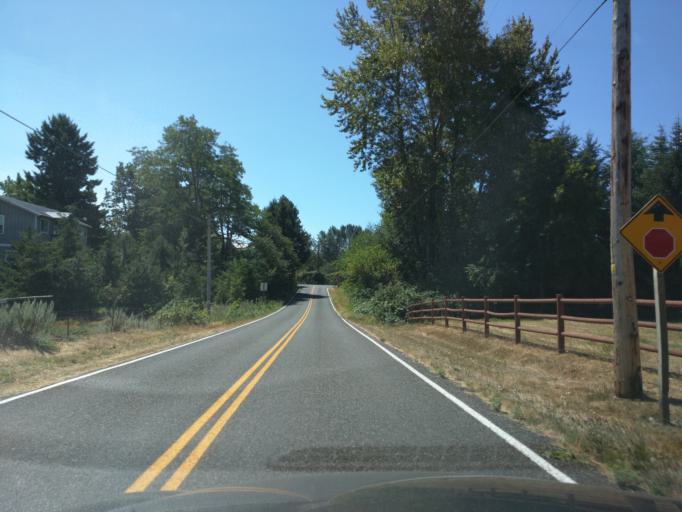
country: US
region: Washington
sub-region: Whatcom County
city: Lynden
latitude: 48.8784
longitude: -122.4148
